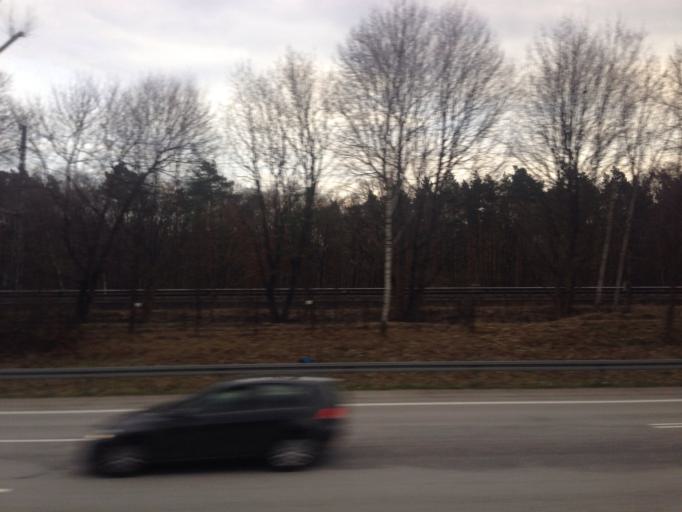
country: DE
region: Berlin
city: Grunewald
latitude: 52.4731
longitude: 13.2414
